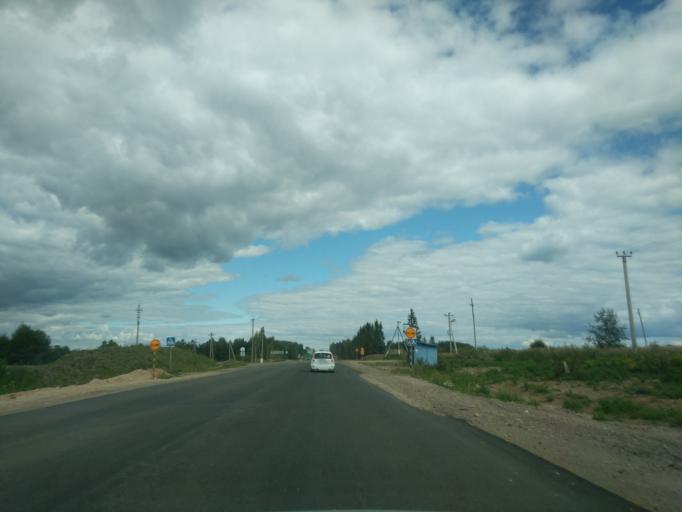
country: RU
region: Kostroma
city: Sudislavl'
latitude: 57.8655
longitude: 41.6296
